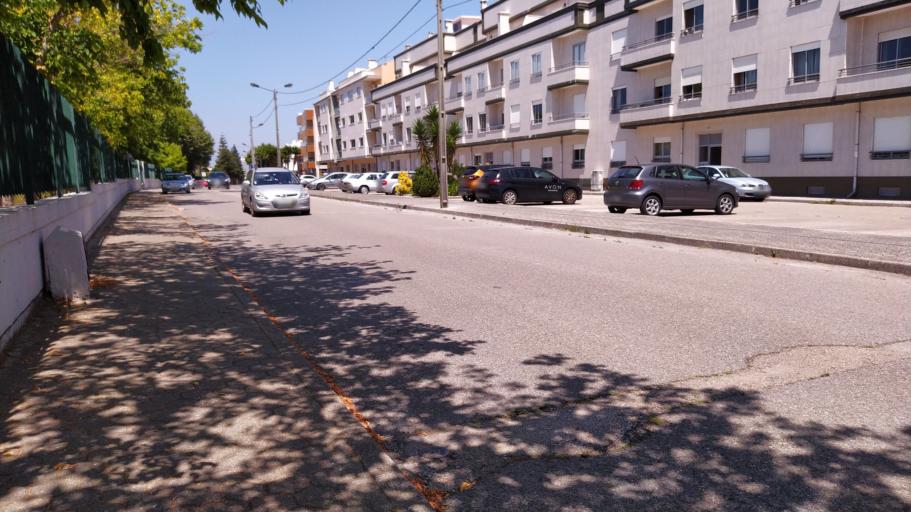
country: PT
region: Aveiro
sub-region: Aveiro
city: Aveiro
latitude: 40.6447
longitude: -8.6314
